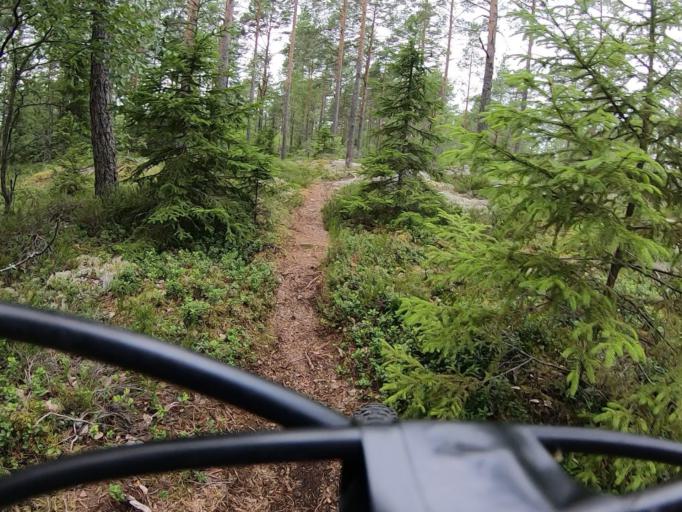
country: FI
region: Varsinais-Suomi
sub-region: Vakka-Suomi
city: Uusikaupunki
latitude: 60.8377
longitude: 21.3958
